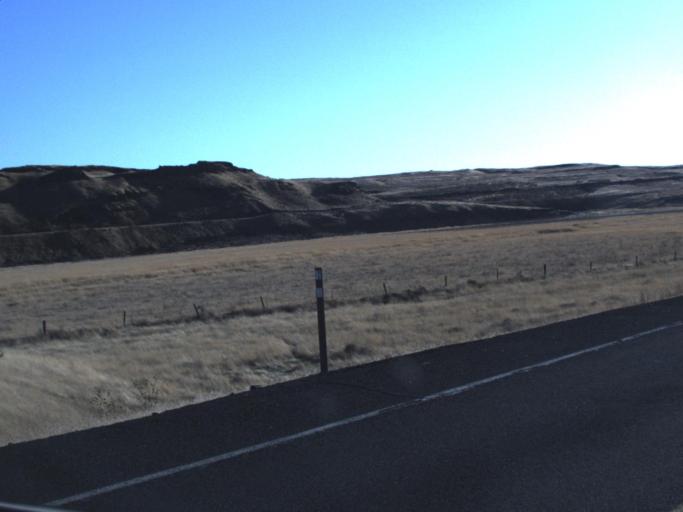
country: US
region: Washington
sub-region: Adams County
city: Ritzville
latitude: 46.7427
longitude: -118.3240
